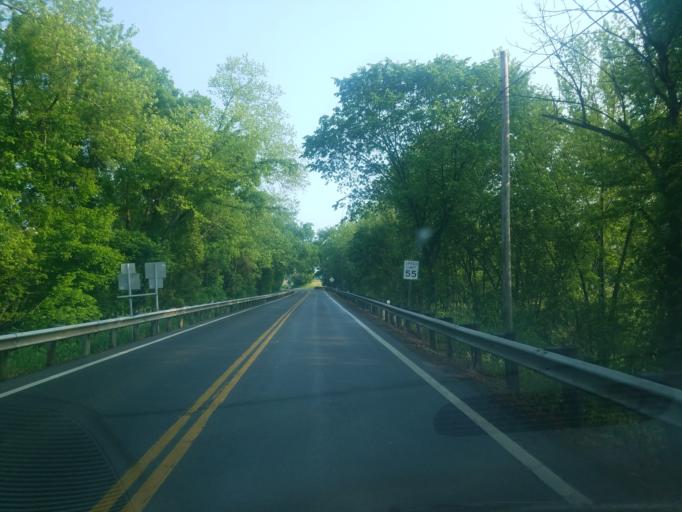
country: US
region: Ohio
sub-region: Tuscarawas County
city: Dover
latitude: 40.5806
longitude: -81.3939
